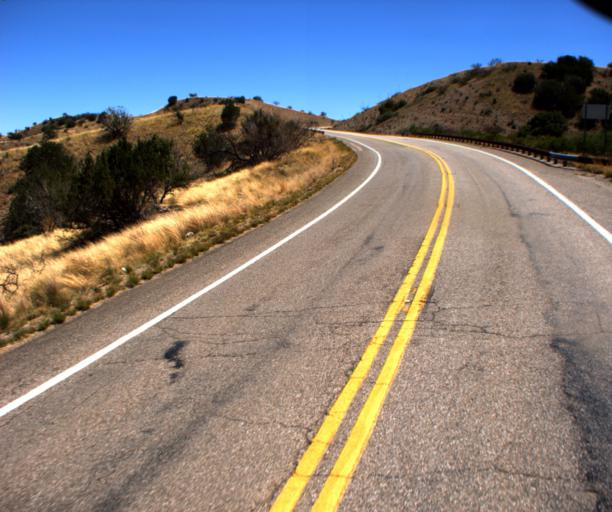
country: US
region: Arizona
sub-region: Pima County
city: Corona de Tucson
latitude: 31.8240
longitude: -110.7141
